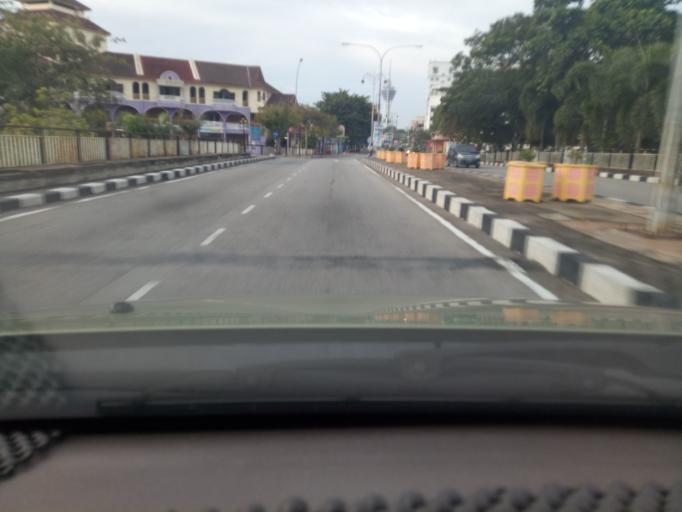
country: MY
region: Kedah
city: Alor Setar
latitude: 6.1147
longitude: 100.3649
